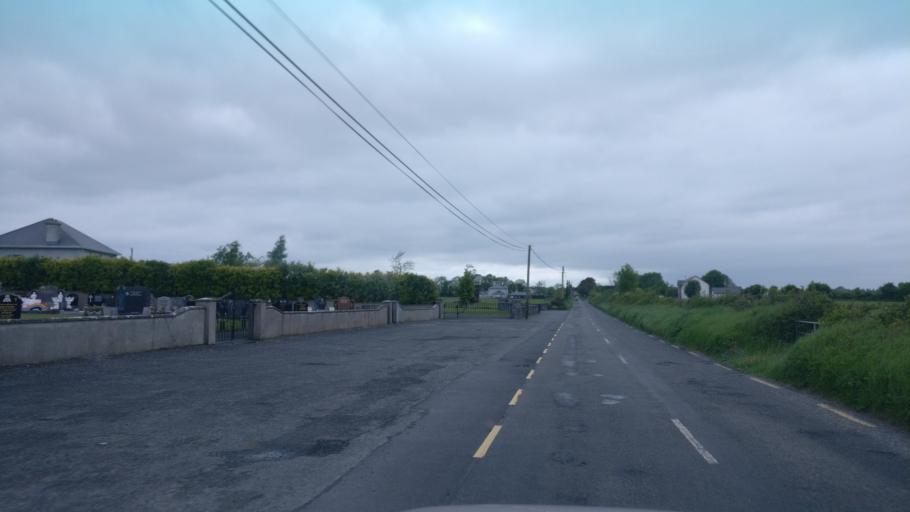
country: IE
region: Connaught
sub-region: County Galway
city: Portumna
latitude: 53.0926
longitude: -8.2359
